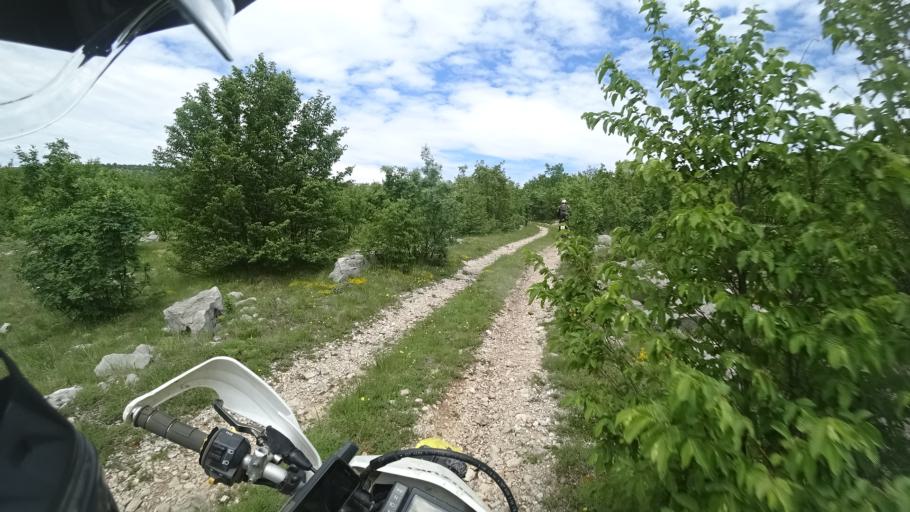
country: HR
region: Splitsko-Dalmatinska
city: Hrvace
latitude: 43.8849
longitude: 16.5889
